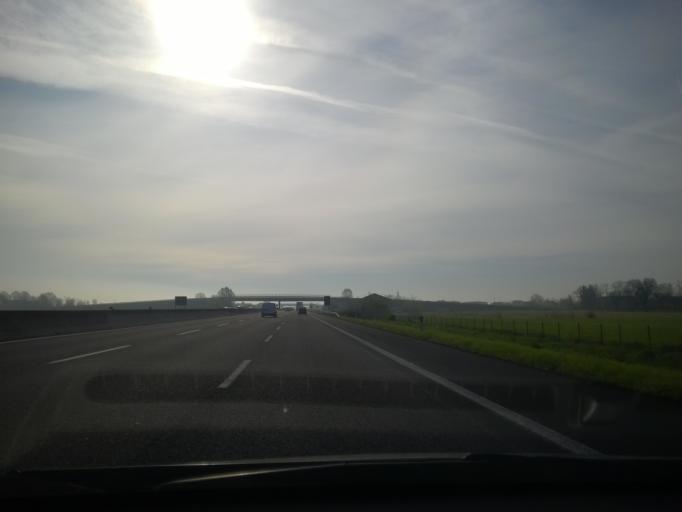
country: IT
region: Emilia-Romagna
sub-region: Provincia di Bologna
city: Castel Guelfo di Bologna
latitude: 44.4030
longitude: 11.6840
